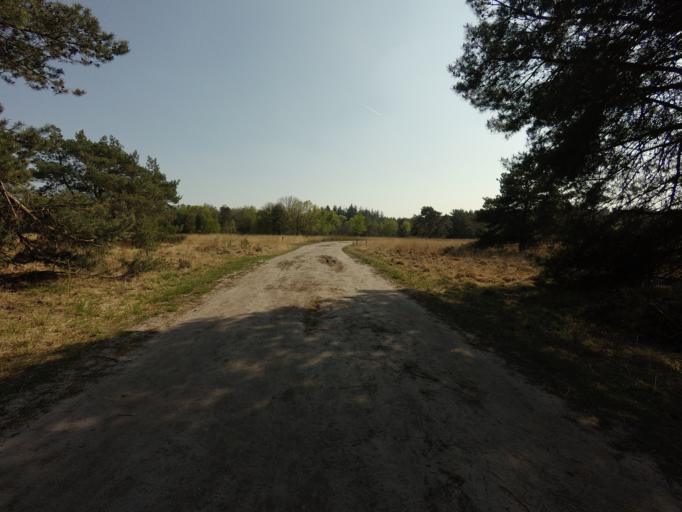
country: NL
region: North Brabant
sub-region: Gemeente Goirle
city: Goirle
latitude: 51.4983
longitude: 5.0244
